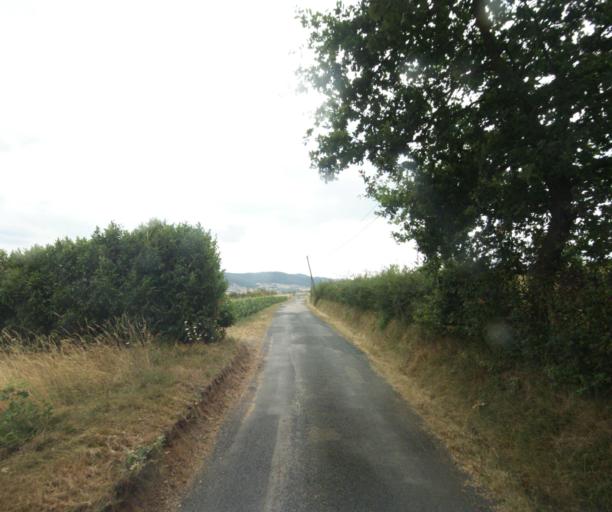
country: FR
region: Rhone-Alpes
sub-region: Departement du Rhone
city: Bully
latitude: 45.8696
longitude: 4.5651
